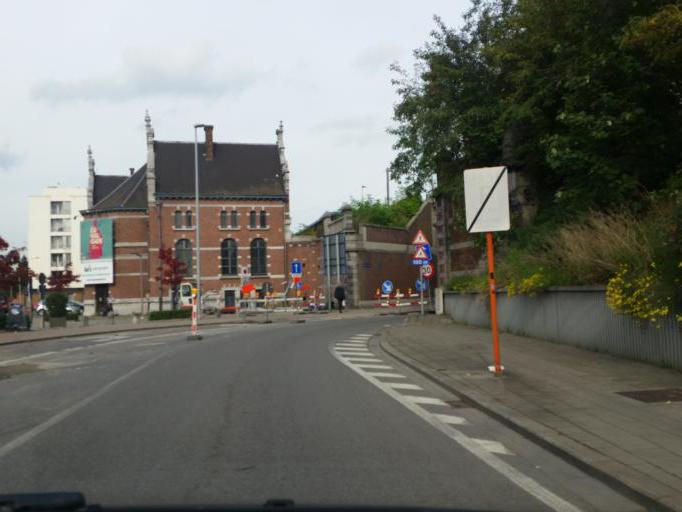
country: BE
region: Flanders
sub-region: Provincie Antwerpen
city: Mechelen
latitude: 51.0292
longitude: 4.4896
